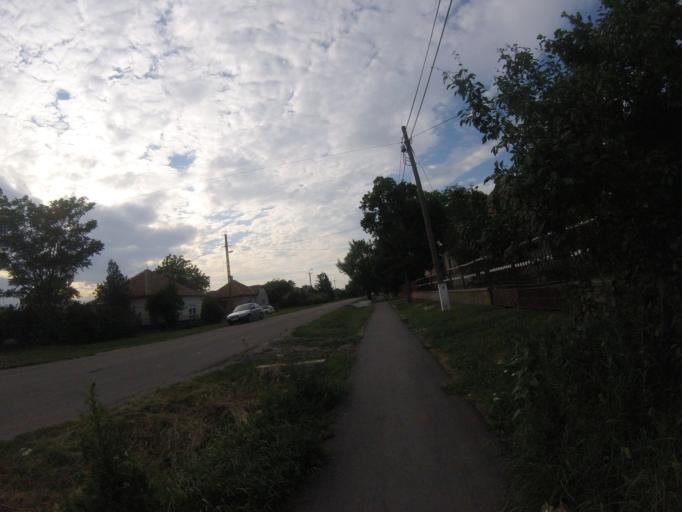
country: HU
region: Heves
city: Tiszanana
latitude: 47.5987
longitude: 20.5871
